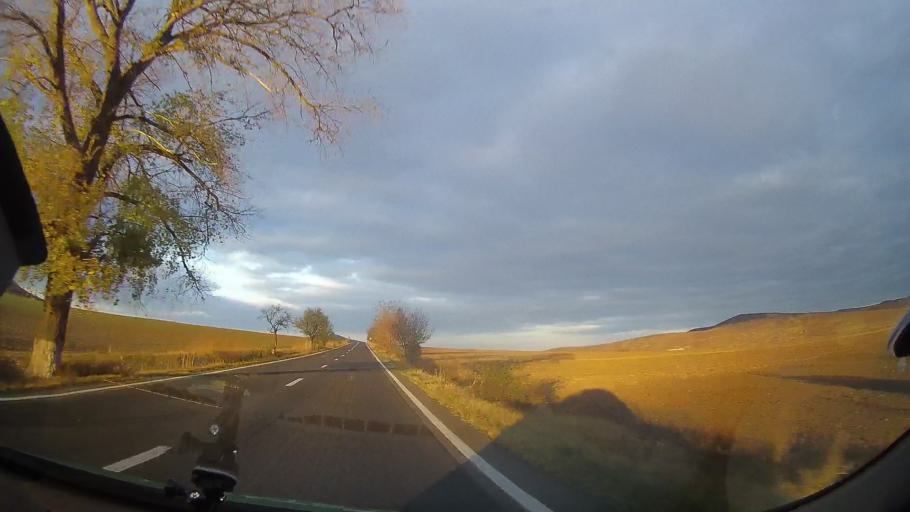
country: RO
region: Tulcea
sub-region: Comuna Nalbant
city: Nicolae Balcescu
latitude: 44.9774
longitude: 28.5461
